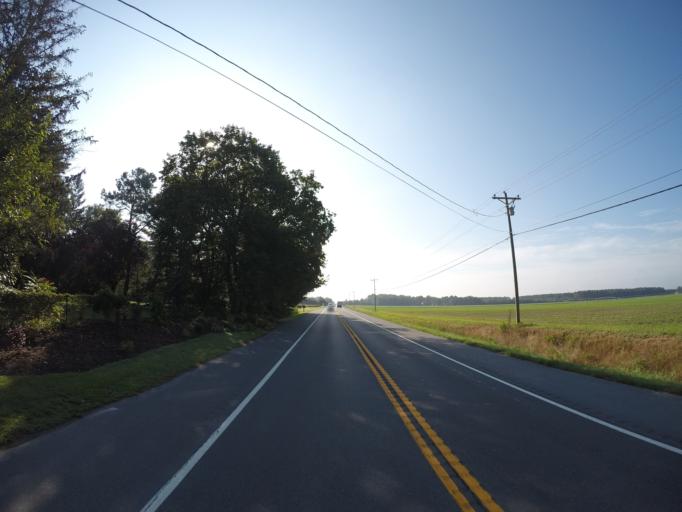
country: US
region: Delaware
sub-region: Sussex County
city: Bridgeville
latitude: 38.7081
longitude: -75.5203
